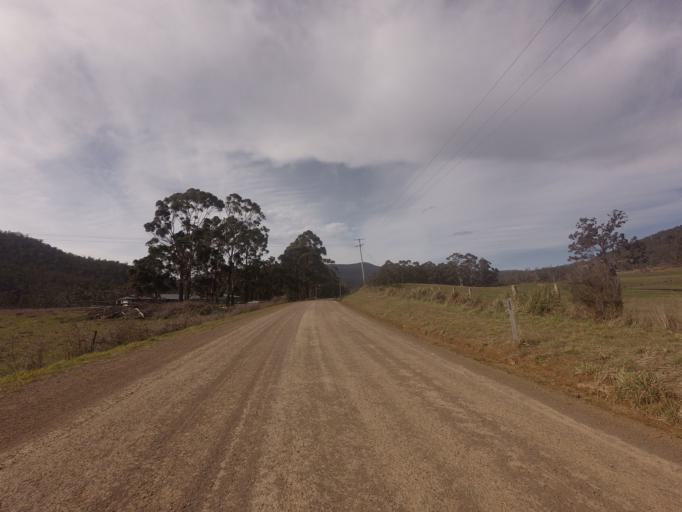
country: AU
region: Tasmania
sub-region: Huon Valley
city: Huonville
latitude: -43.0723
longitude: 147.0490
